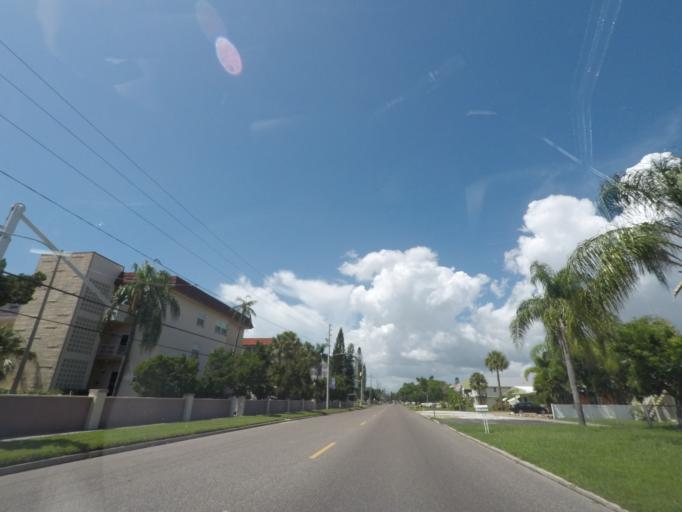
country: US
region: Florida
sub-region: Pinellas County
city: Gulfport
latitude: 27.7393
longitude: -82.7115
